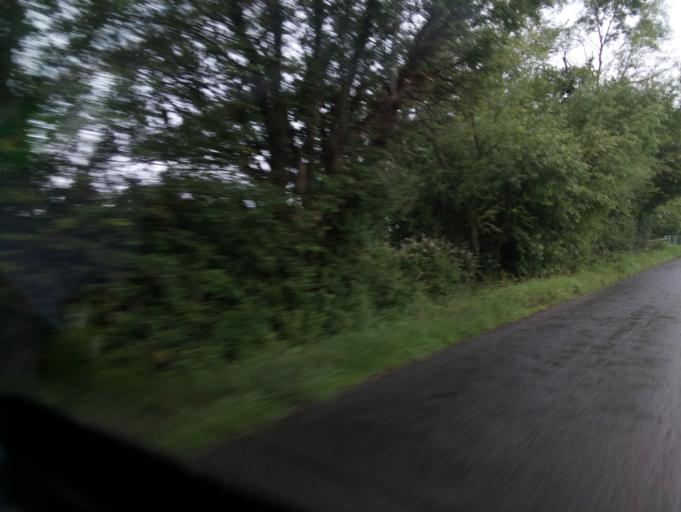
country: GB
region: England
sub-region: Gloucestershire
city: Uckington
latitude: 51.9344
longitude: -2.1194
